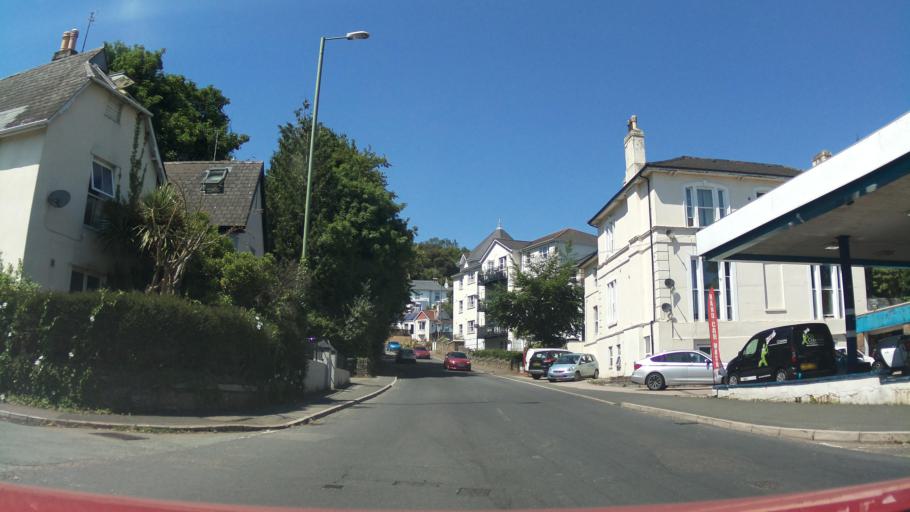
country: GB
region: England
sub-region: Borough of Torbay
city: Torquay
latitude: 50.4720
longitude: -3.5448
